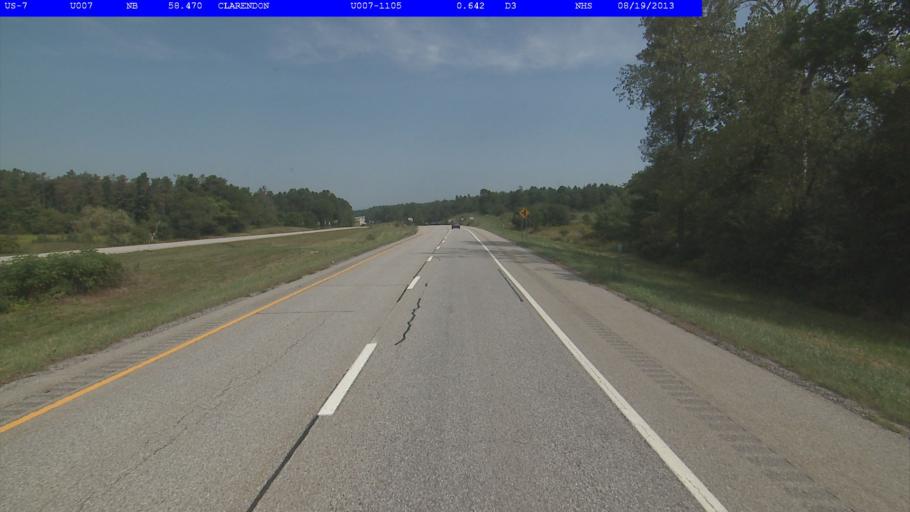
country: US
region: Vermont
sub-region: Rutland County
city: Rutland
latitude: 43.5032
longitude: -72.9673
